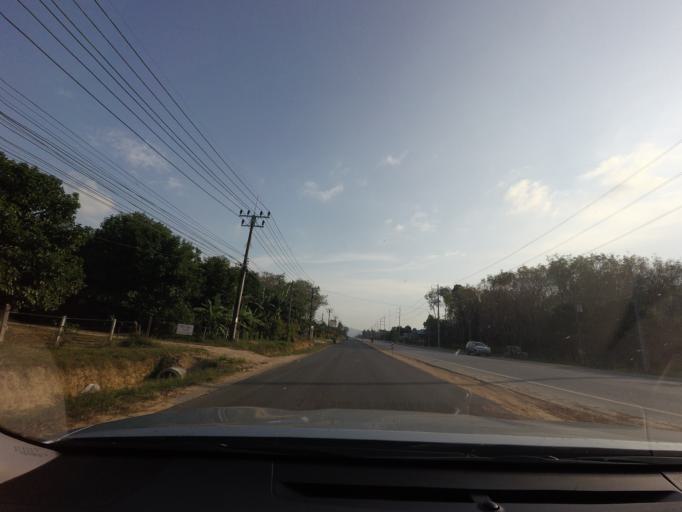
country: TH
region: Phangnga
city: Ban Khao Lak
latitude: 8.7310
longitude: 98.2555
